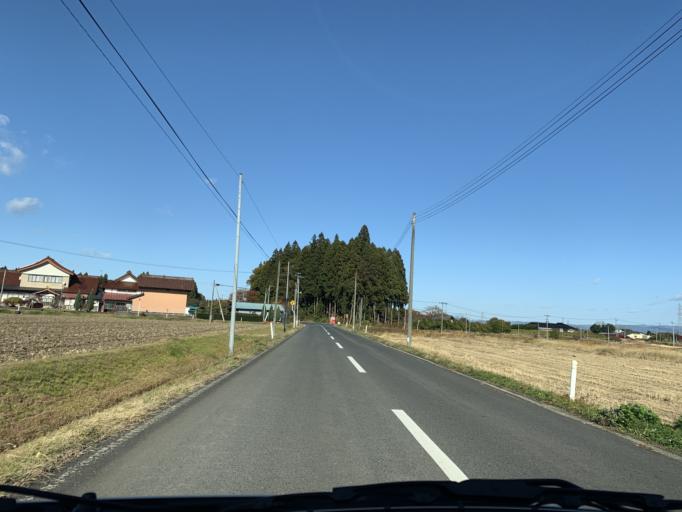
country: JP
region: Iwate
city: Mizusawa
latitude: 39.0785
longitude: 141.1210
